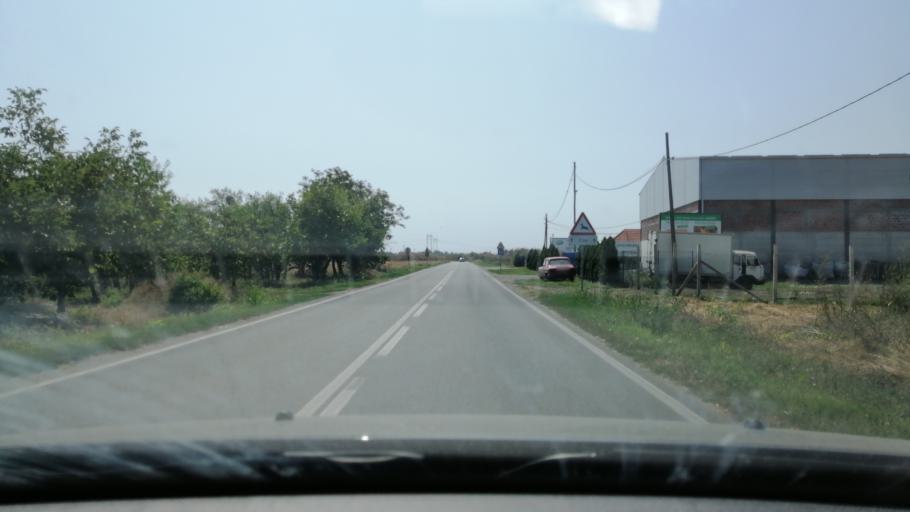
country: RS
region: Autonomna Pokrajina Vojvodina
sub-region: Juznobanatski Okrug
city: Pancevo
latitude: 44.7954
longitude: 20.7198
